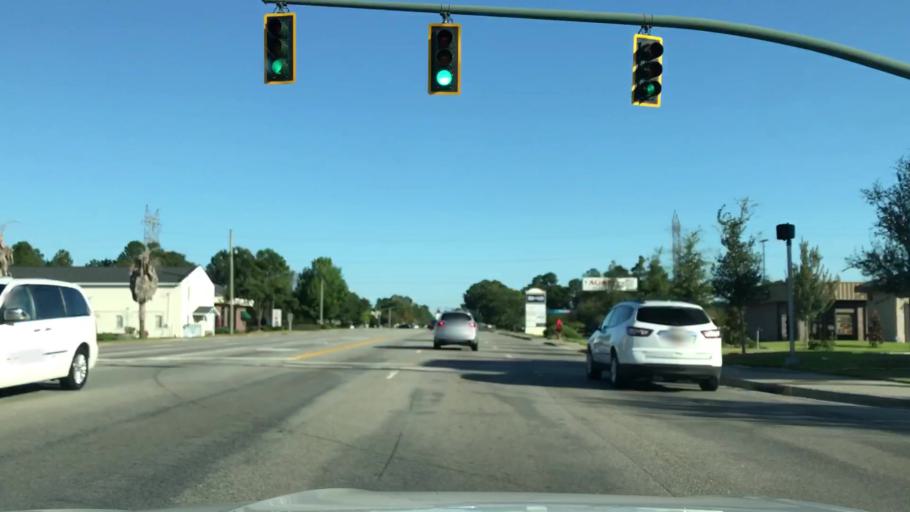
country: US
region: South Carolina
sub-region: Berkeley County
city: Goose Creek
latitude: 33.0019
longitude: -80.0418
